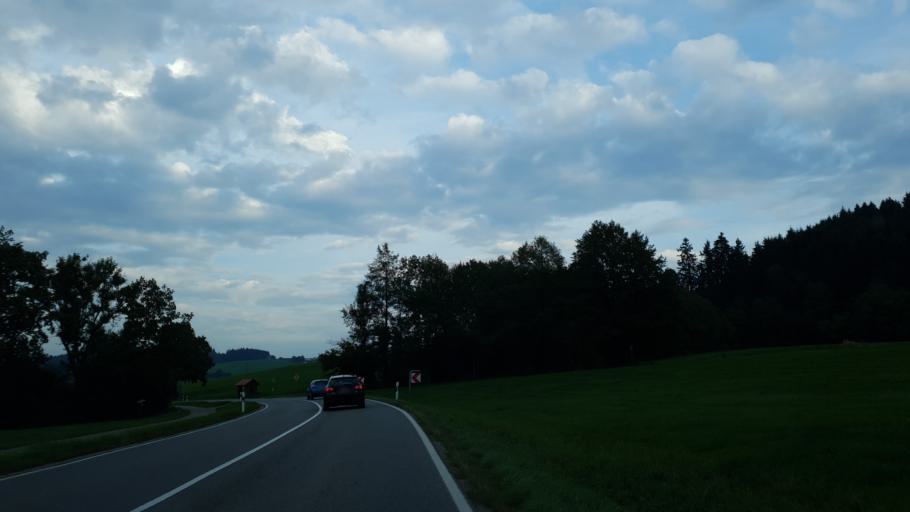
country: DE
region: Bavaria
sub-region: Swabia
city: Gestratz
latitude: 47.6786
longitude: 9.9813
